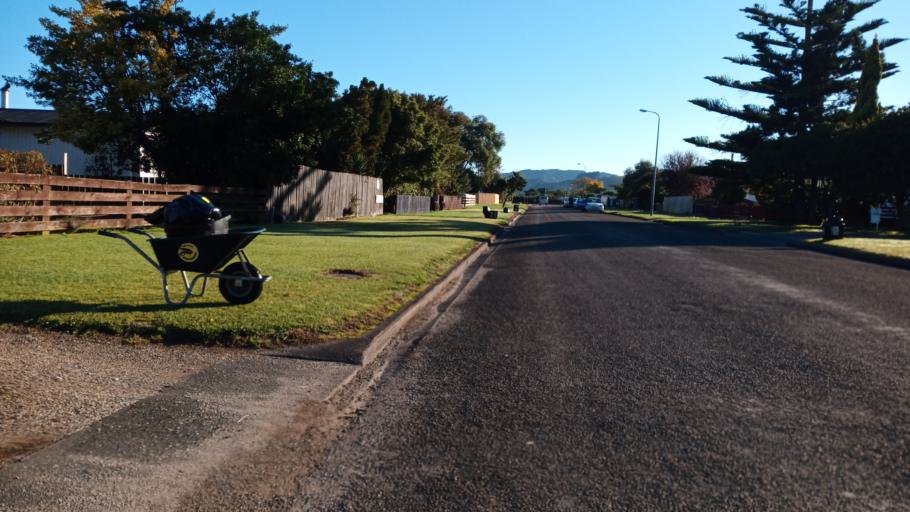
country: NZ
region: Gisborne
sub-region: Gisborne District
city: Gisborne
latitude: -38.6604
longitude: 178.0013
